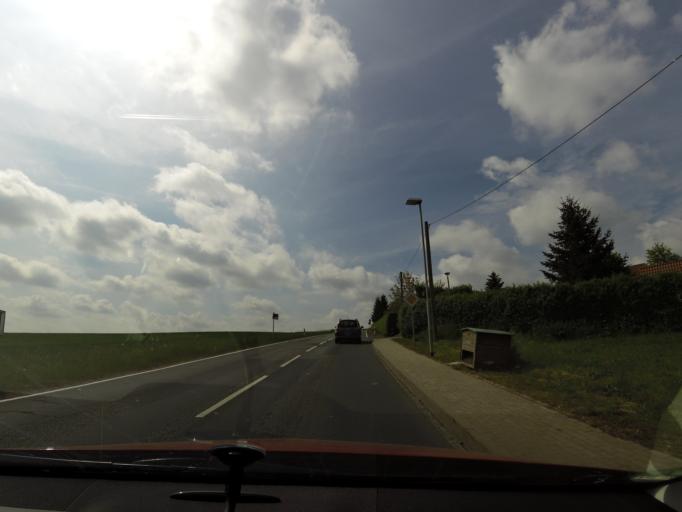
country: DE
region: Thuringia
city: Mihla
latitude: 51.0736
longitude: 10.3254
